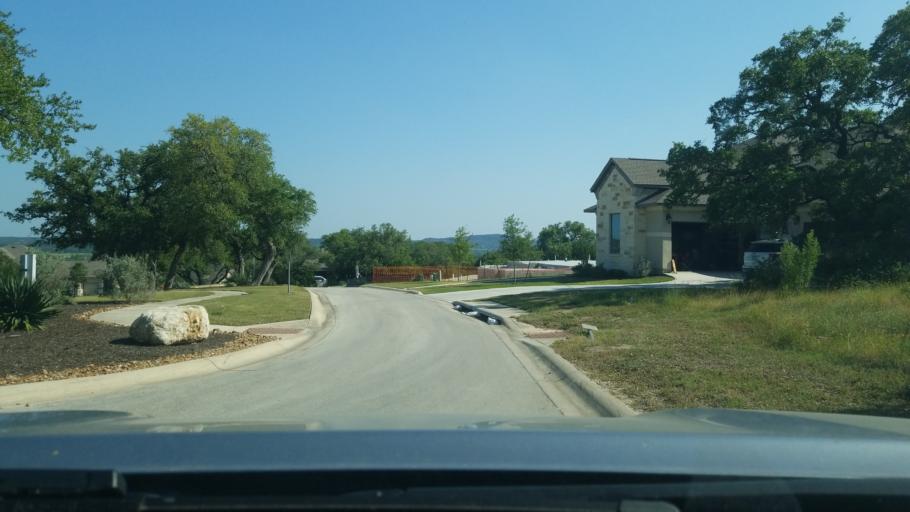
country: US
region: Texas
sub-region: Comal County
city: Bulverde
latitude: 29.7624
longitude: -98.4215
